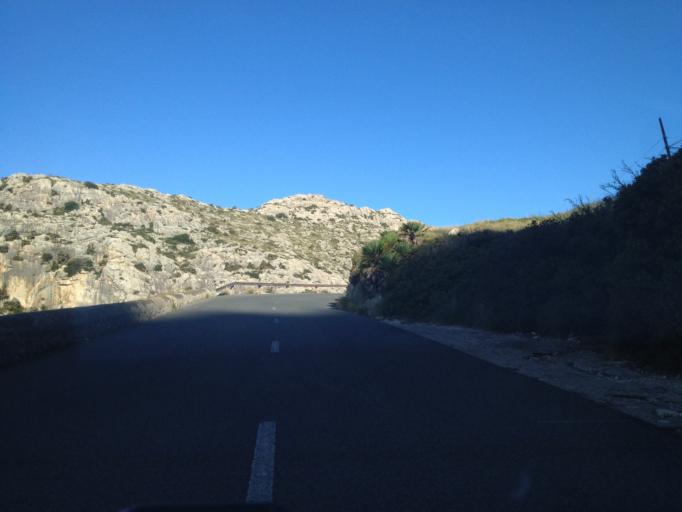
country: ES
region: Balearic Islands
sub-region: Illes Balears
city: Alcudia
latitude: 39.9239
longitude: 3.1076
